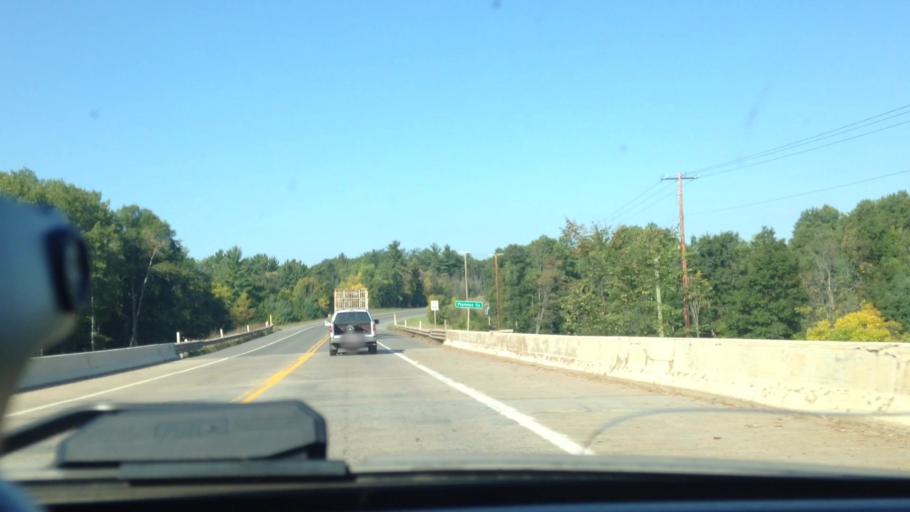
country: US
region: Michigan
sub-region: Dickinson County
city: Iron Mountain
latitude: 45.8662
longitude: -88.0744
